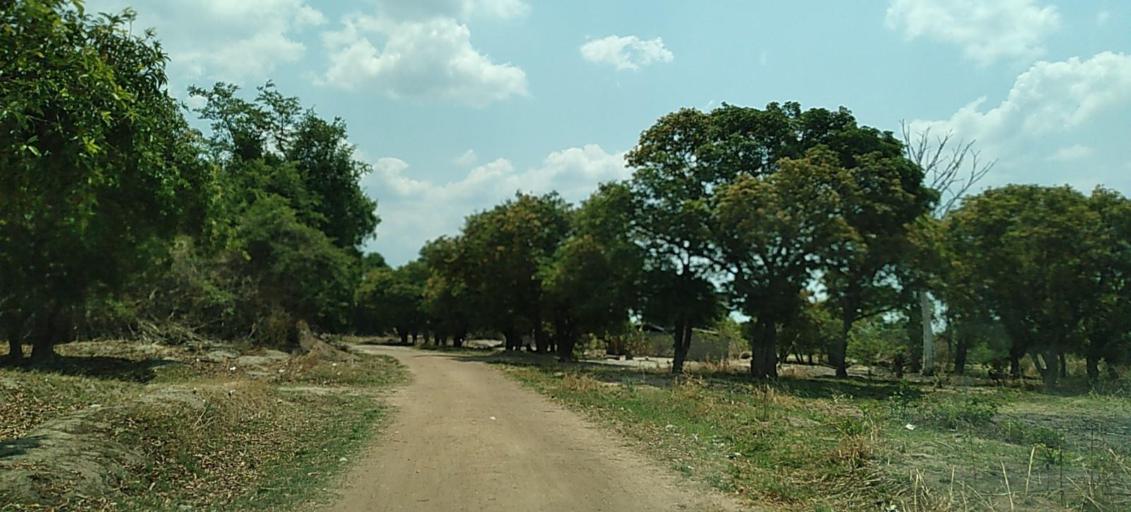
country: ZM
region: Copperbelt
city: Luanshya
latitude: -13.1555
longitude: 28.3139
